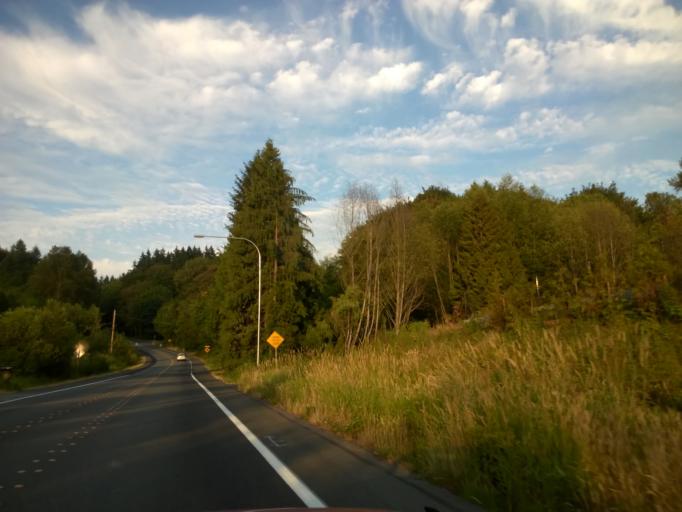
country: US
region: Washington
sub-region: King County
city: Redmond
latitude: 47.7111
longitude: -122.1251
